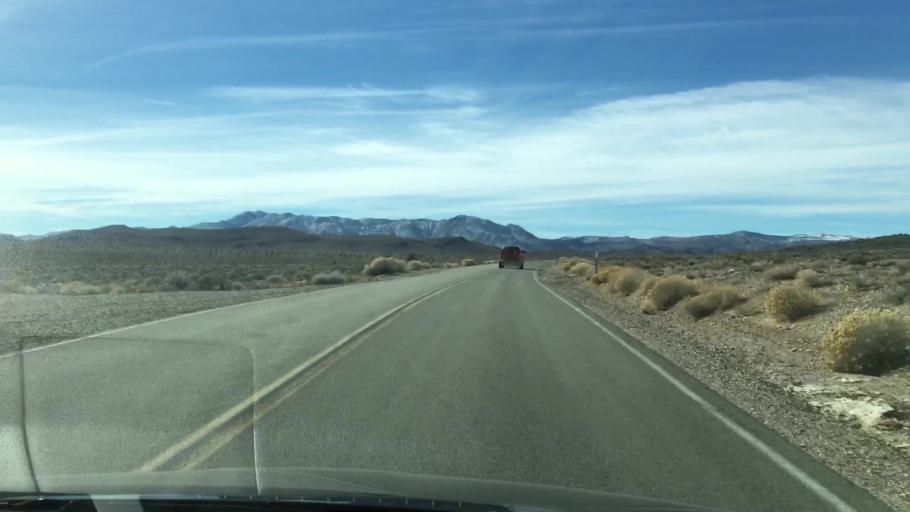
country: US
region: California
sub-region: Inyo County
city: Lone Pine
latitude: 36.3288
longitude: -117.6571
